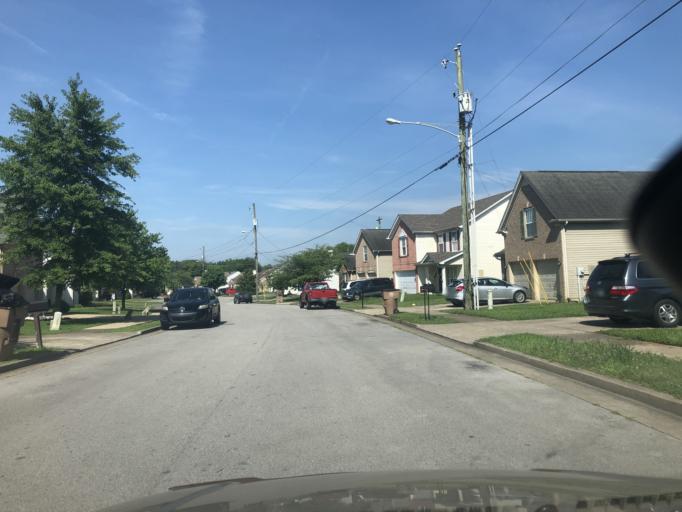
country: US
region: Tennessee
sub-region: Davidson County
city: Lakewood
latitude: 36.2407
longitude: -86.7031
